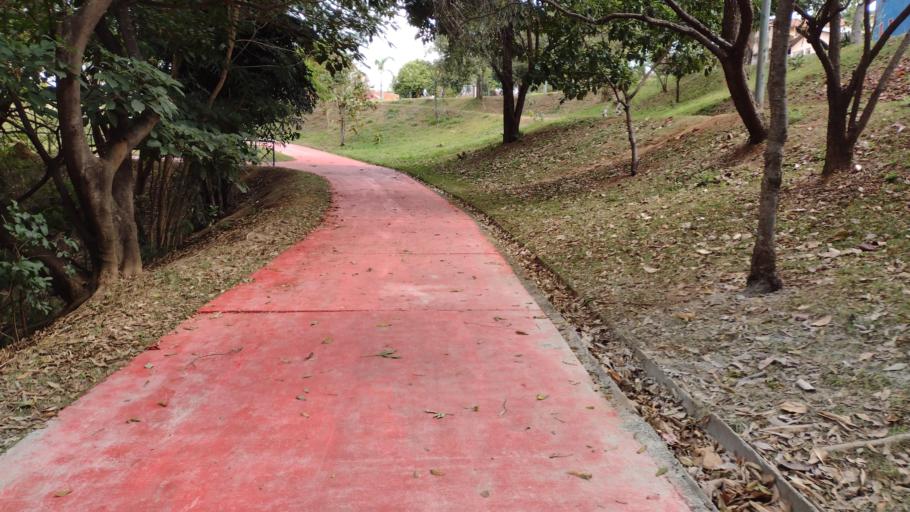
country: BR
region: Sao Paulo
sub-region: Sorocaba
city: Sorocaba
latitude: -23.4624
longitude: -47.4740
